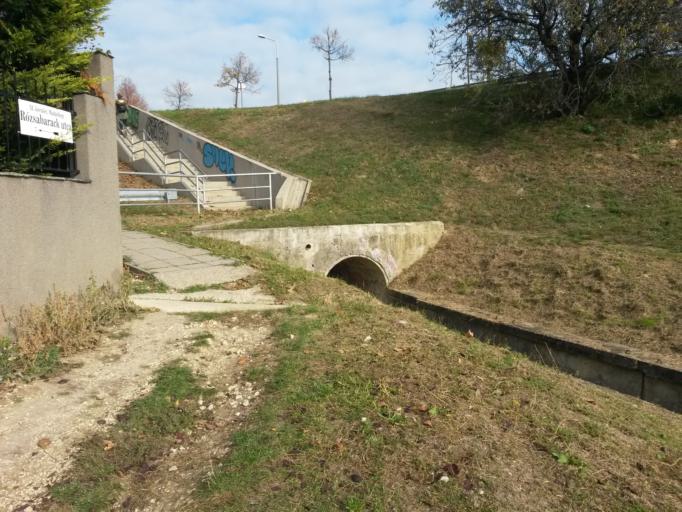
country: HU
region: Budapest
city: Budapest XII. keruelet
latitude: 47.4732
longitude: 18.9914
